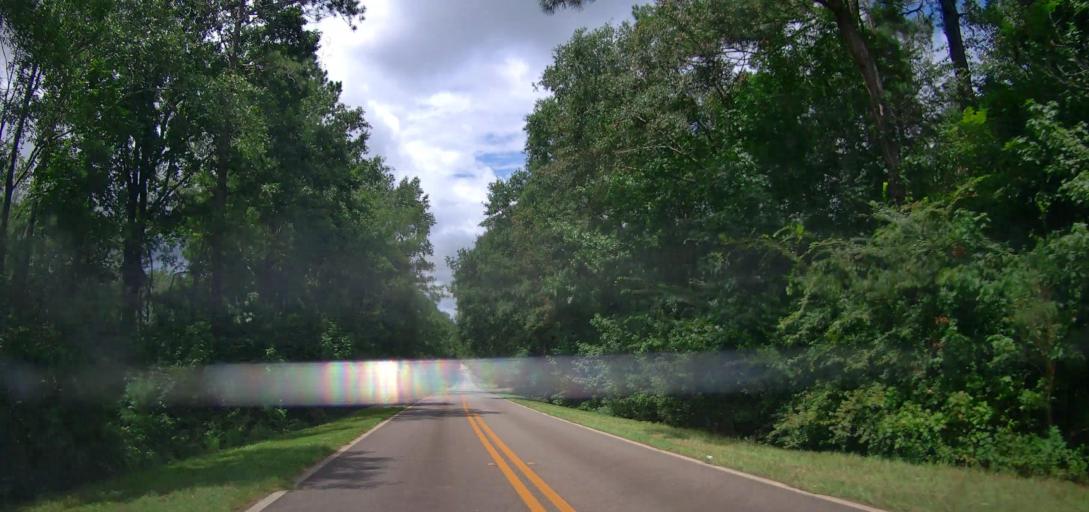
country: US
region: Georgia
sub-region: Pulaski County
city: Hawkinsville
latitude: 32.3338
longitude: -83.5308
